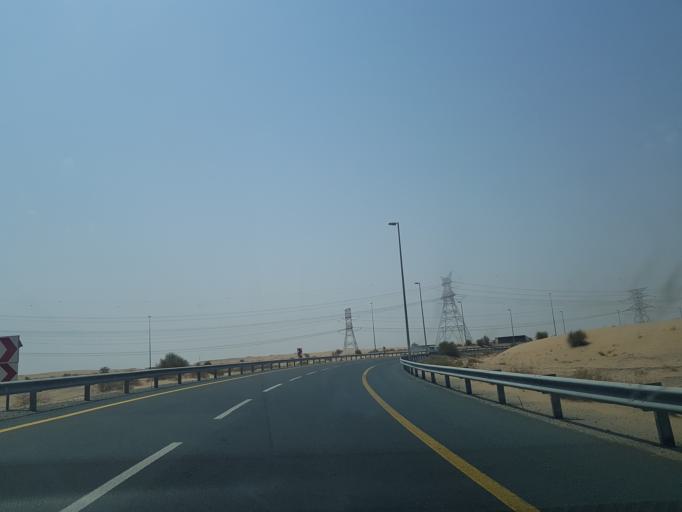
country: AE
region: Ash Shariqah
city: Sharjah
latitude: 25.1161
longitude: 55.4298
